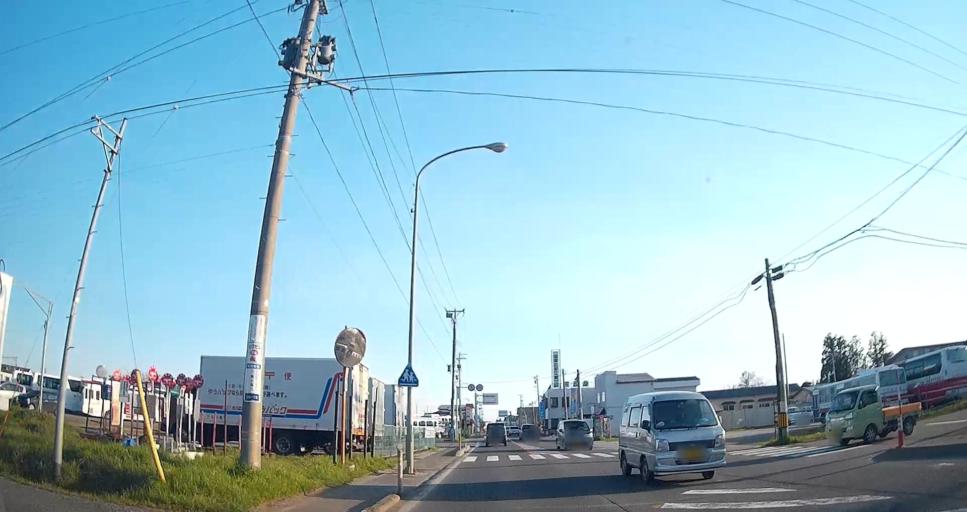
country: JP
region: Aomori
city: Mutsu
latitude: 41.2830
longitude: 141.2105
